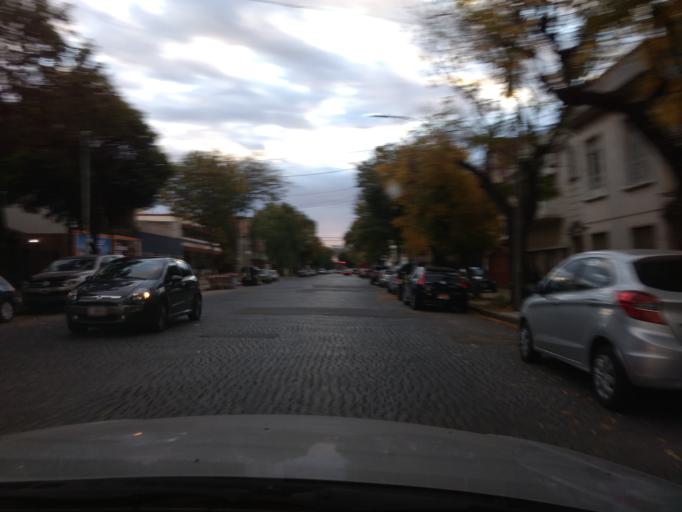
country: AR
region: Buenos Aires F.D.
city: Villa Santa Rita
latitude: -34.6323
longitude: -58.4953
